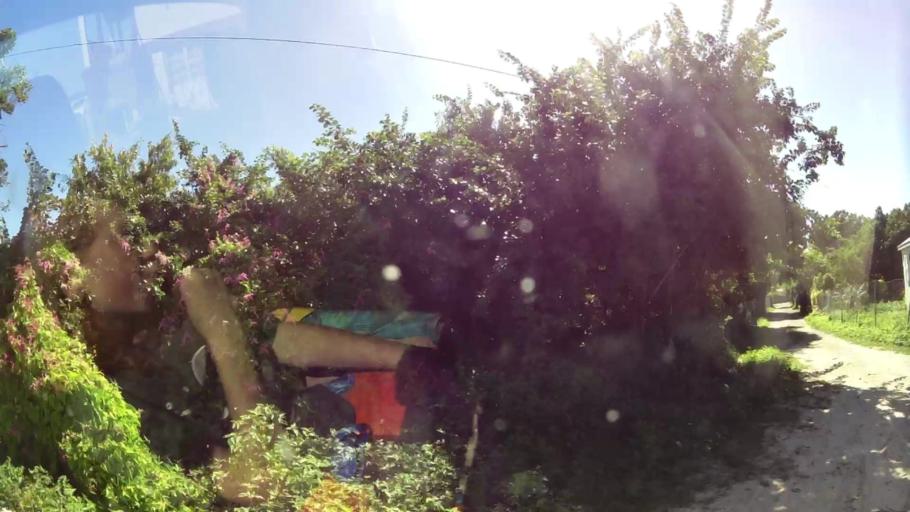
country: AG
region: Barbuda
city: Codrington
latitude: 17.6403
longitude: -61.8267
